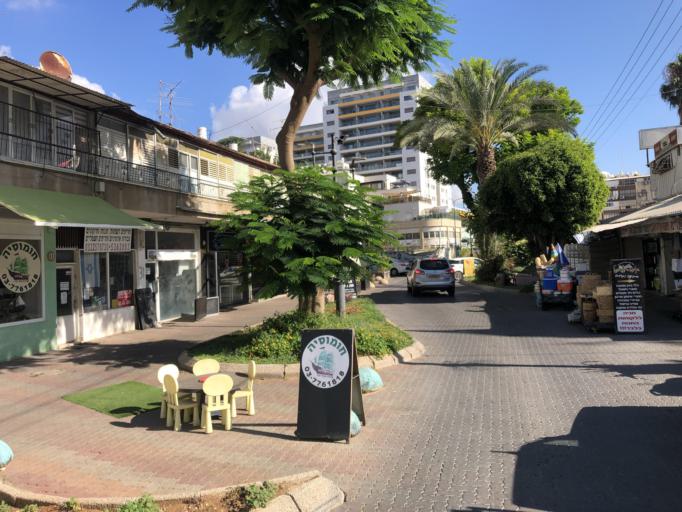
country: IL
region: Central District
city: Yehud
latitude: 32.0308
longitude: 34.8887
